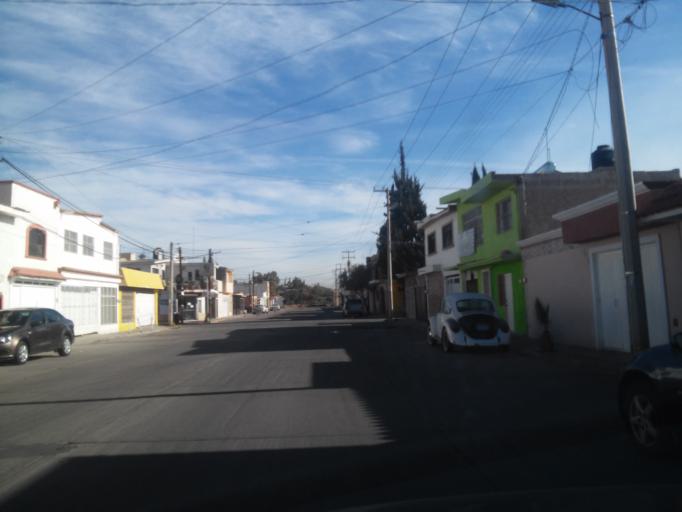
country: MX
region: Durango
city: Victoria de Durango
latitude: 24.0424
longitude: -104.6530
